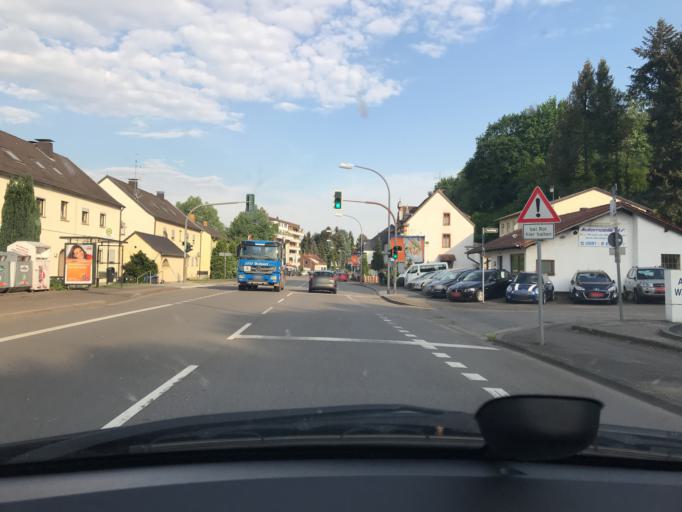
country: FR
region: Lorraine
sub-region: Departement de la Moselle
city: Alsting
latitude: 49.1976
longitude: 7.0197
